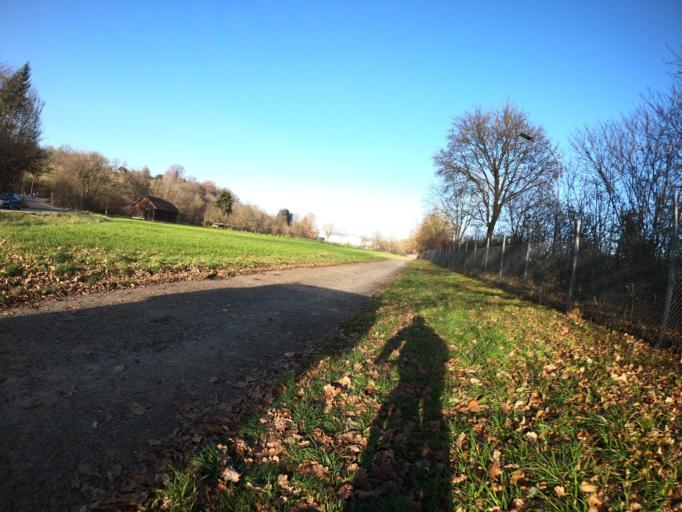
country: DE
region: Baden-Wuerttemberg
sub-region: Regierungsbezirk Stuttgart
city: Goeppingen
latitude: 48.6857
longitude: 9.6711
